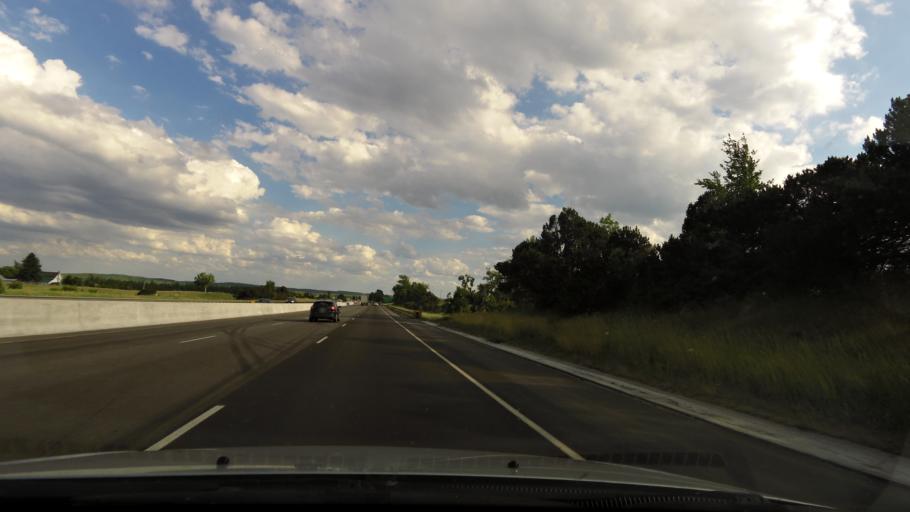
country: CA
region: Ontario
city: Innisfil
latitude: 44.2161
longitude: -79.6613
